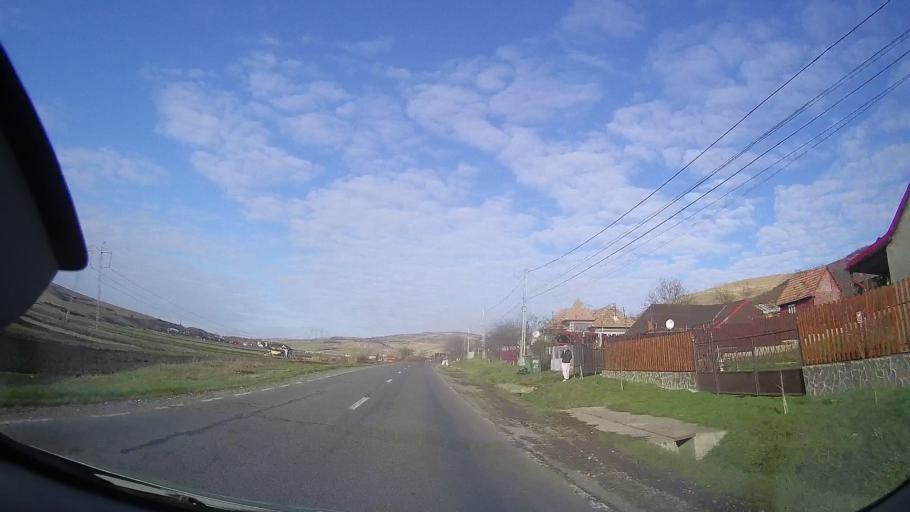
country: RO
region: Cluj
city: Caianu Mic
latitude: 46.8026
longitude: 23.8739
